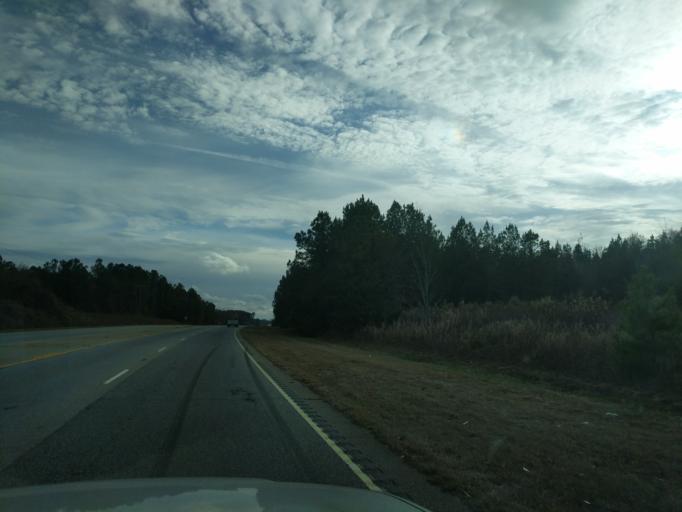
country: US
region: South Carolina
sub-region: Anderson County
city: Honea Path
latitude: 34.5494
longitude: -82.3179
